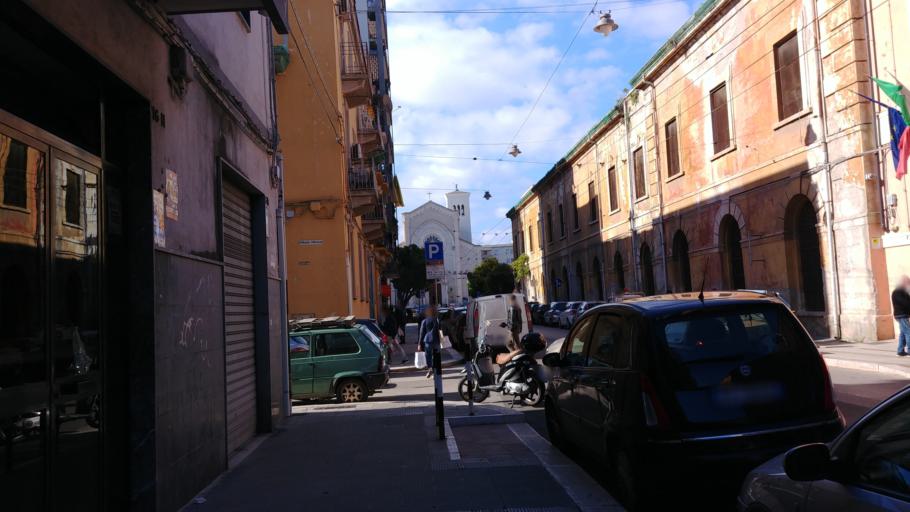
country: IT
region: Apulia
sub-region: Provincia di Bari
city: Bari
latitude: 41.1192
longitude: 16.8574
